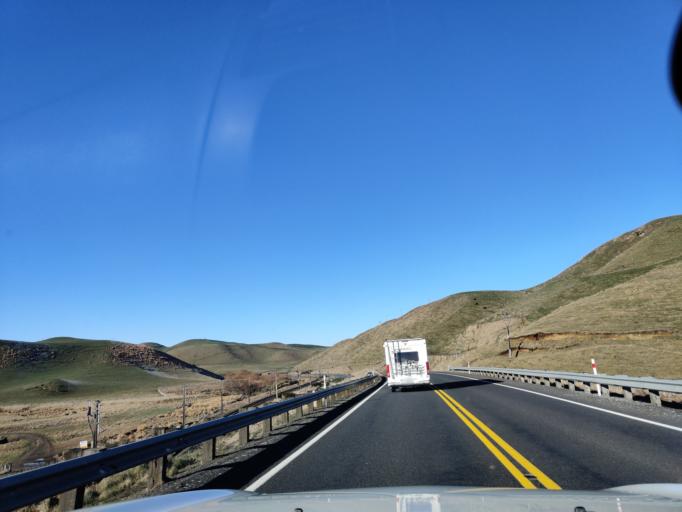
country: NZ
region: Manawatu-Wanganui
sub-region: Ruapehu District
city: Waiouru
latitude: -39.5001
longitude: 175.6739
